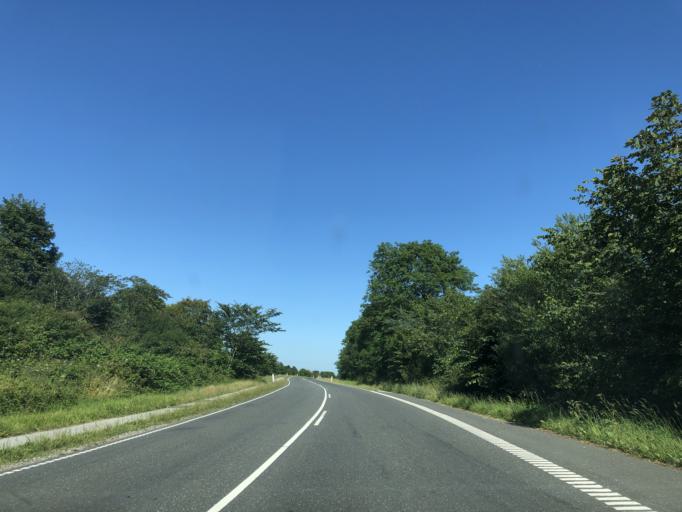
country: DK
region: Central Jutland
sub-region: Syddjurs Kommune
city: Ronde
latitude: 56.2994
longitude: 10.4896
